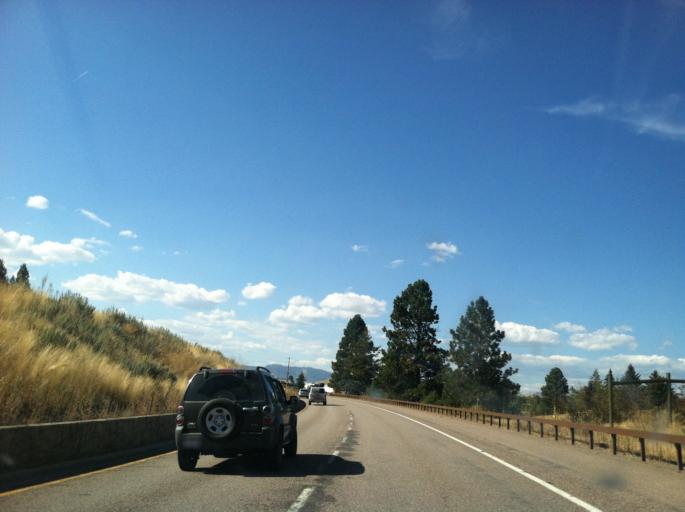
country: US
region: Montana
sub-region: Lake County
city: Polson
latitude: 47.6775
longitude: -114.1095
